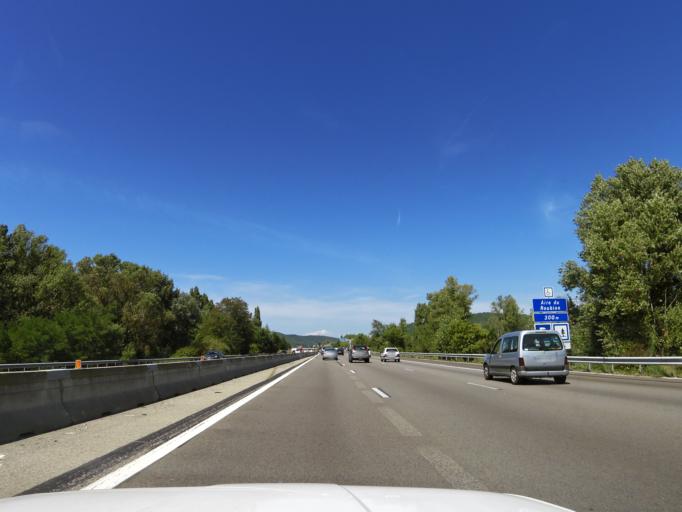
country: FR
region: Rhone-Alpes
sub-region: Departement de la Drome
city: Saint-Marcel-les-Sauzet
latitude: 44.5857
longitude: 4.8028
